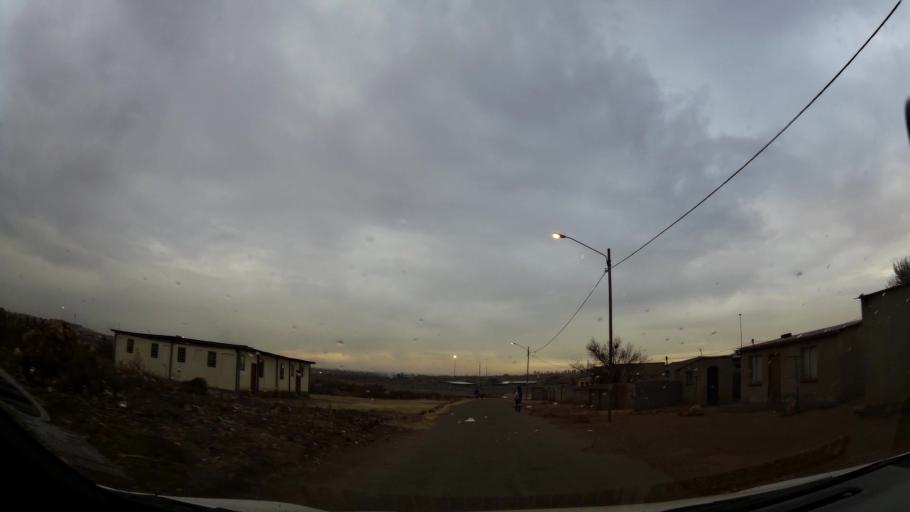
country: ZA
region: Gauteng
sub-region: Ekurhuleni Metropolitan Municipality
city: Germiston
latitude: -26.3845
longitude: 28.1721
